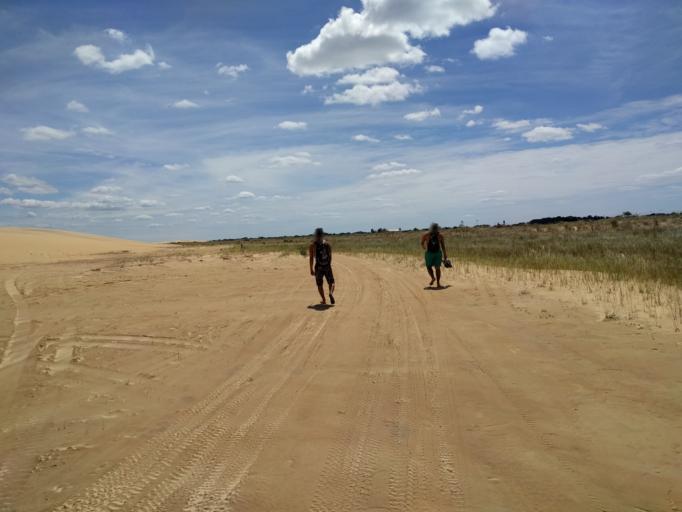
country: BO
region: Santa Cruz
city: Santa Cruz de la Sierra
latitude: -17.9421
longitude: -63.1541
